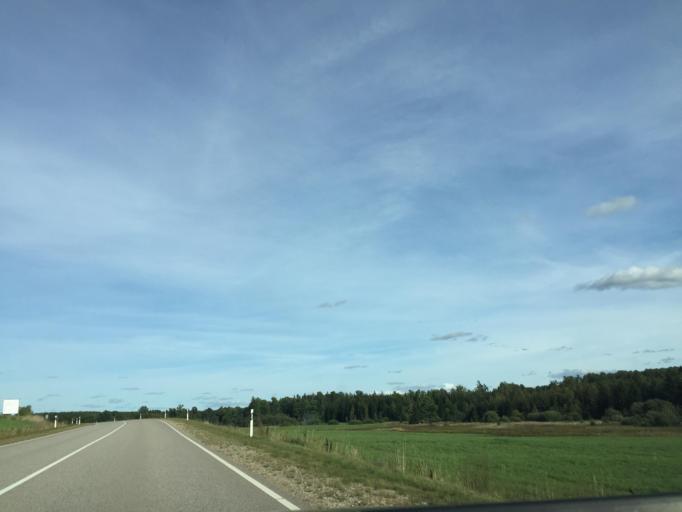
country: LV
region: Kandava
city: Kandava
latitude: 56.9392
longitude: 22.6975
